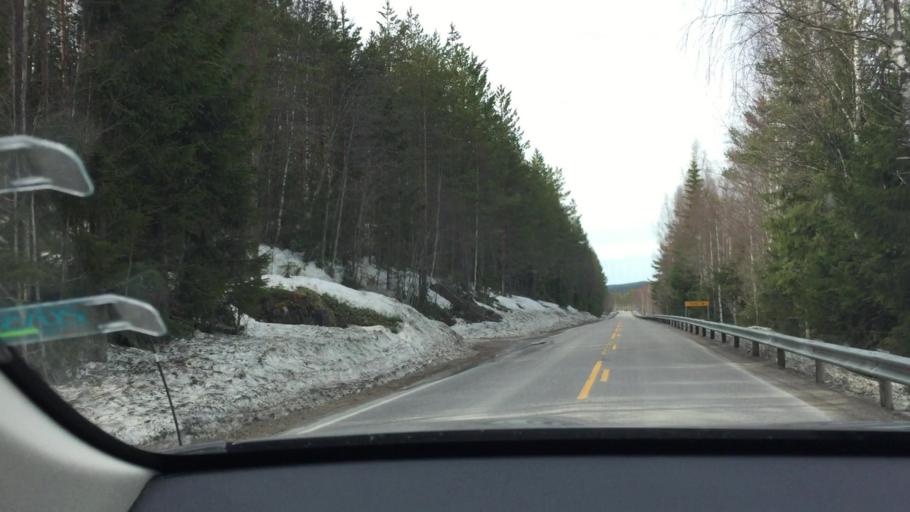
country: NO
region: Hedmark
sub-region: Trysil
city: Innbygda
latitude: 61.0669
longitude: 12.5798
